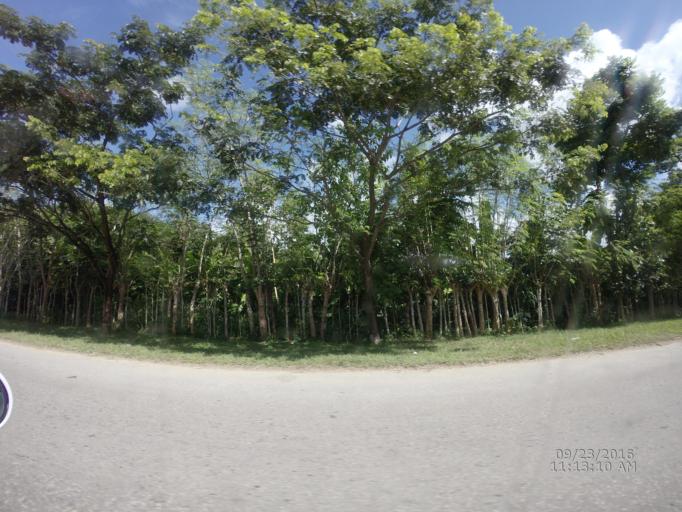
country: CU
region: La Habana
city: Arroyo Naranjo
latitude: 23.0302
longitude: -82.2937
